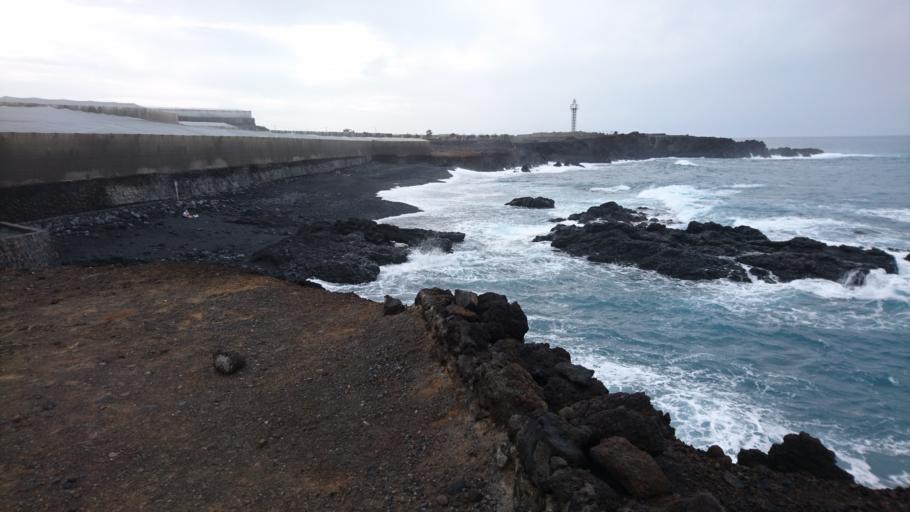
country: ES
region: Canary Islands
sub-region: Provincia de Santa Cruz de Tenerife
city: Tazacorte
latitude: 28.6027
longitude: -17.9238
